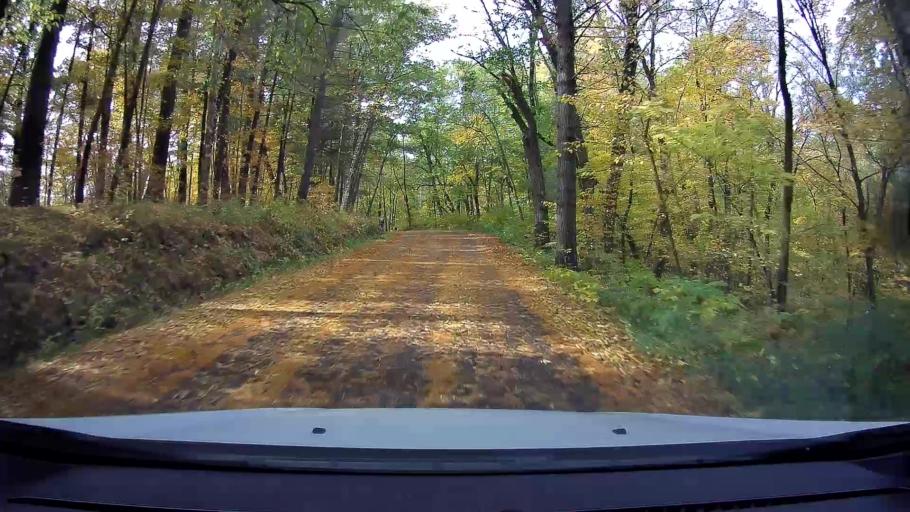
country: US
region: Wisconsin
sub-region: Polk County
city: Saint Croix Falls
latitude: 45.3886
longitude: -92.6561
